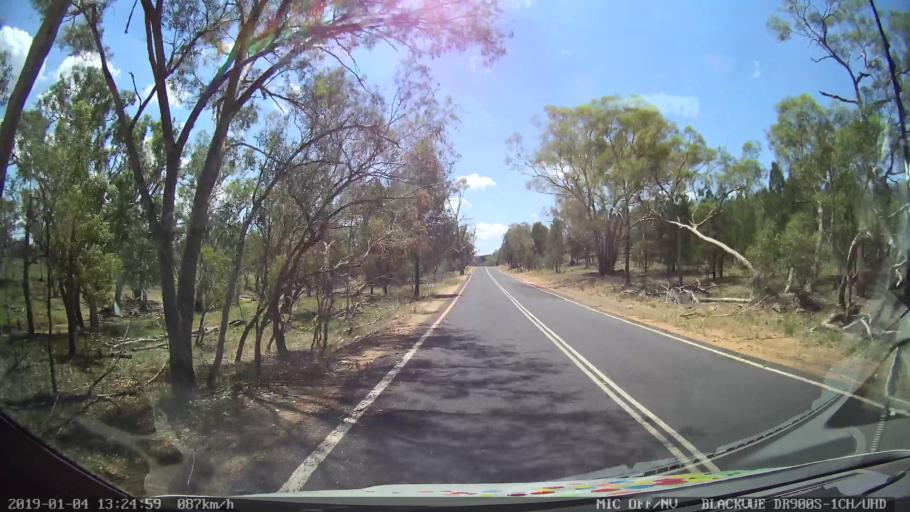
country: AU
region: New South Wales
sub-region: Parkes
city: Peak Hill
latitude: -32.6988
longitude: 148.5540
